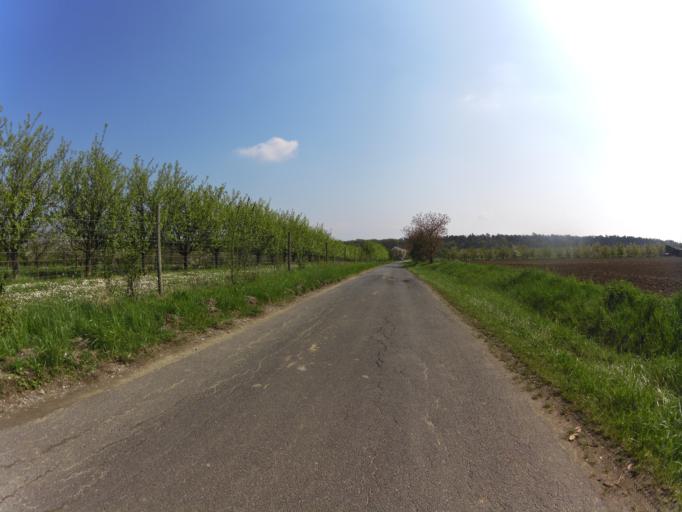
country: DE
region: Bavaria
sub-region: Regierungsbezirk Unterfranken
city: Sommerhausen
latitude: 49.7108
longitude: 10.0512
